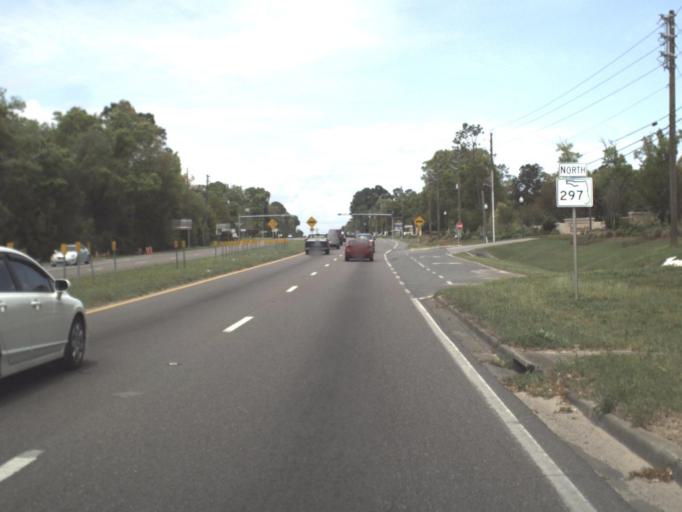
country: US
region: Florida
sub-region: Escambia County
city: Bellview
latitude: 30.4876
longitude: -87.3063
